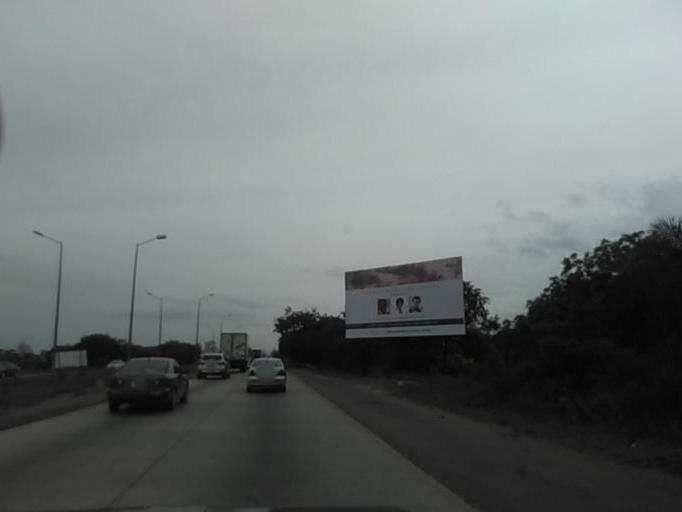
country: GH
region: Greater Accra
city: Medina Estates
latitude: 5.6296
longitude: -0.1565
